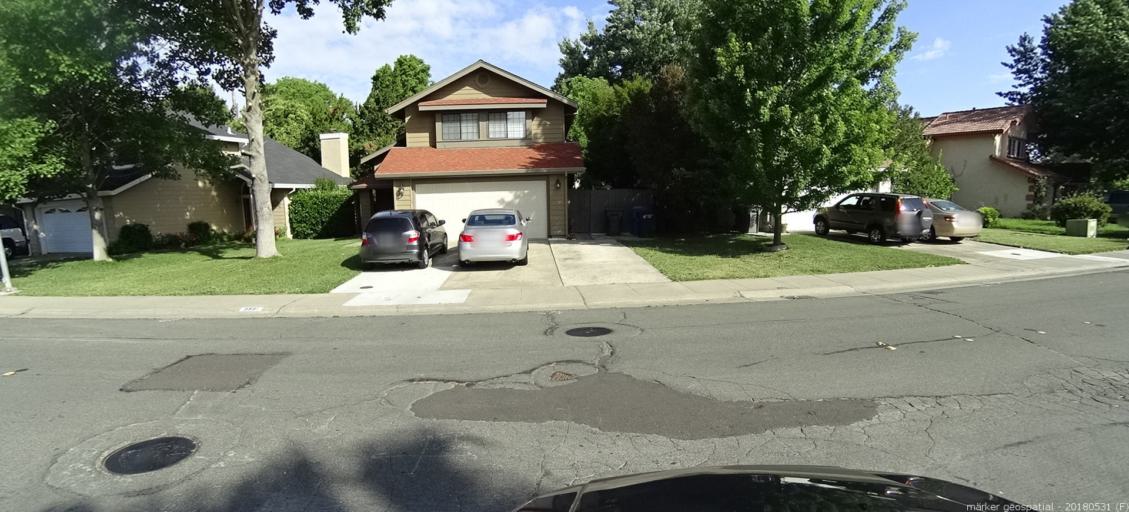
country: US
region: California
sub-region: Sacramento County
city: Sacramento
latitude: 38.6327
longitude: -121.4853
